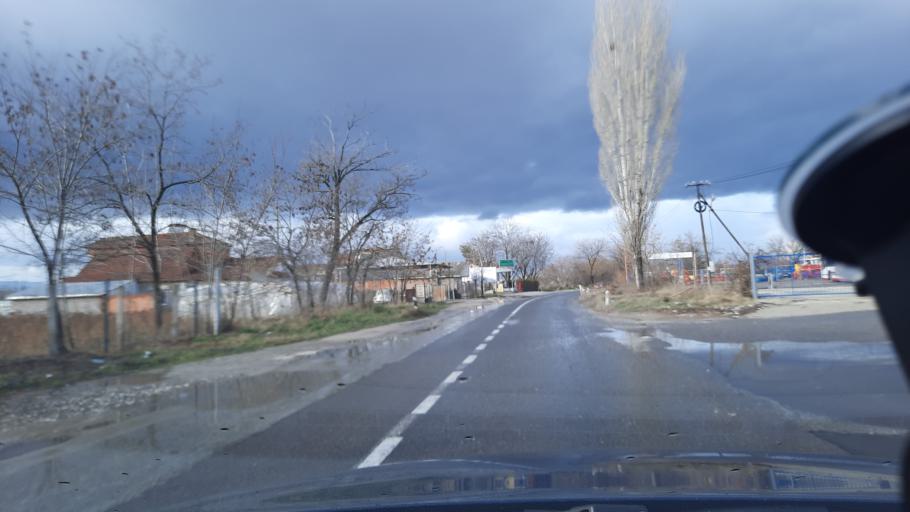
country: MK
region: Prilep
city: Markov Grad
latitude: 41.3430
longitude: 21.5217
